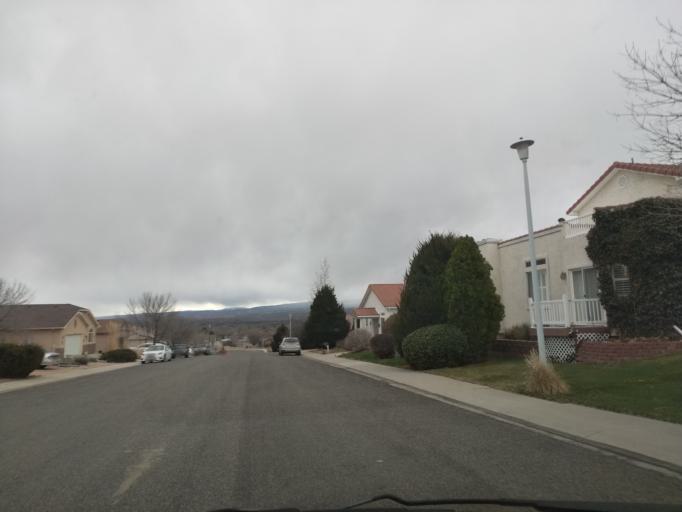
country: US
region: Colorado
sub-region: Mesa County
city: Fruitvale
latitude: 39.0901
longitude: -108.5245
